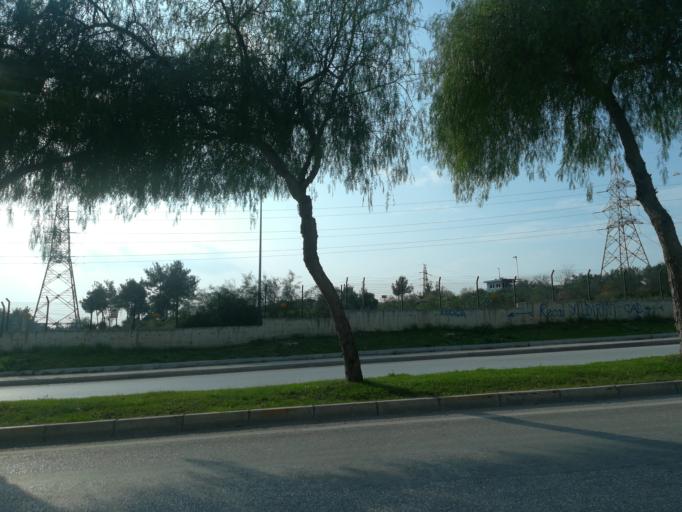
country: TR
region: Adana
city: Adana
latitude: 37.0317
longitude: 35.3461
